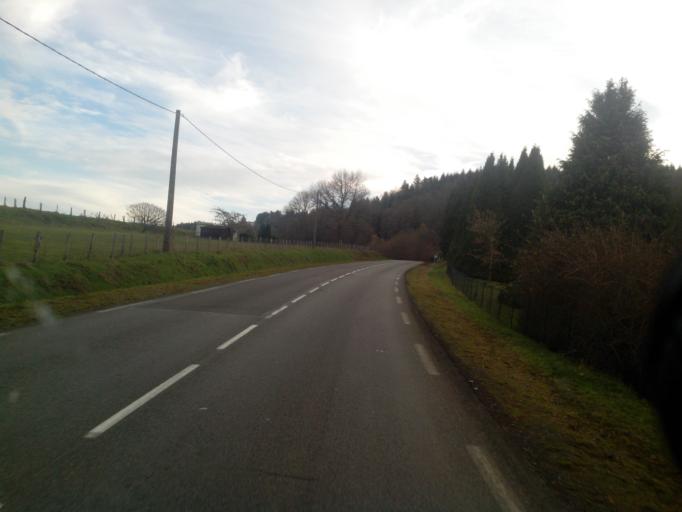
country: FR
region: Limousin
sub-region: Departement de la Haute-Vienne
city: Eymoutiers
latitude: 45.7262
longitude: 1.7555
